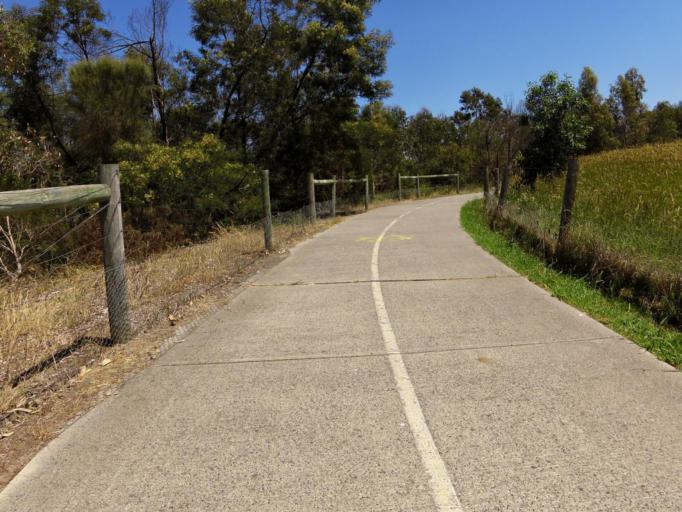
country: AU
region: Victoria
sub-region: Casey
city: Eumemmerring
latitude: -37.9946
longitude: 145.2607
